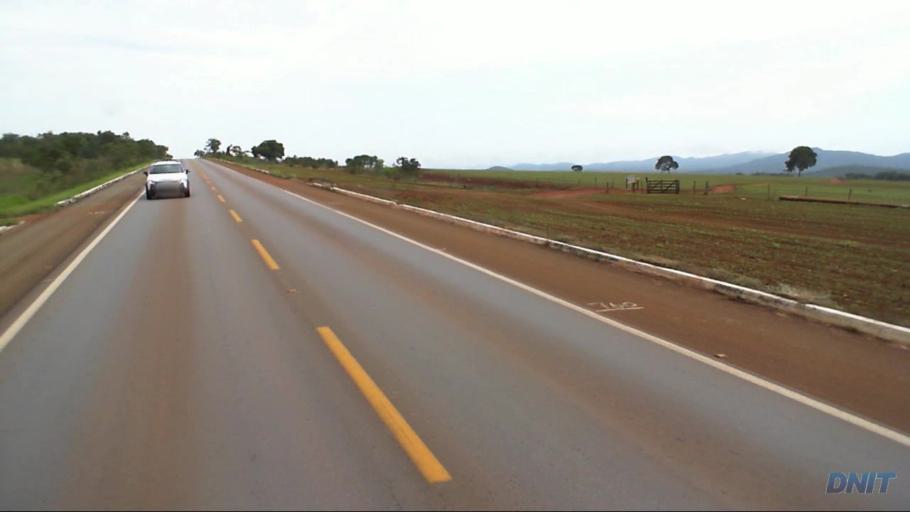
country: BR
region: Goias
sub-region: Uruacu
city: Uruacu
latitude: -14.6808
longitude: -49.1362
